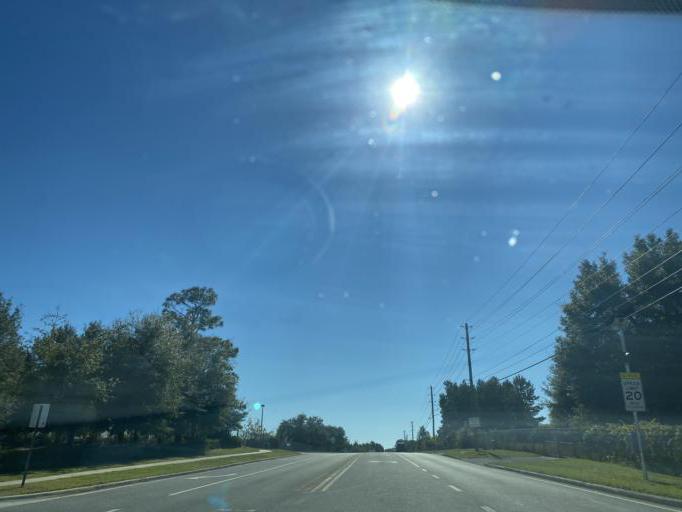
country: US
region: Florida
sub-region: Lake County
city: Lady Lake
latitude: 28.9313
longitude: -81.9370
